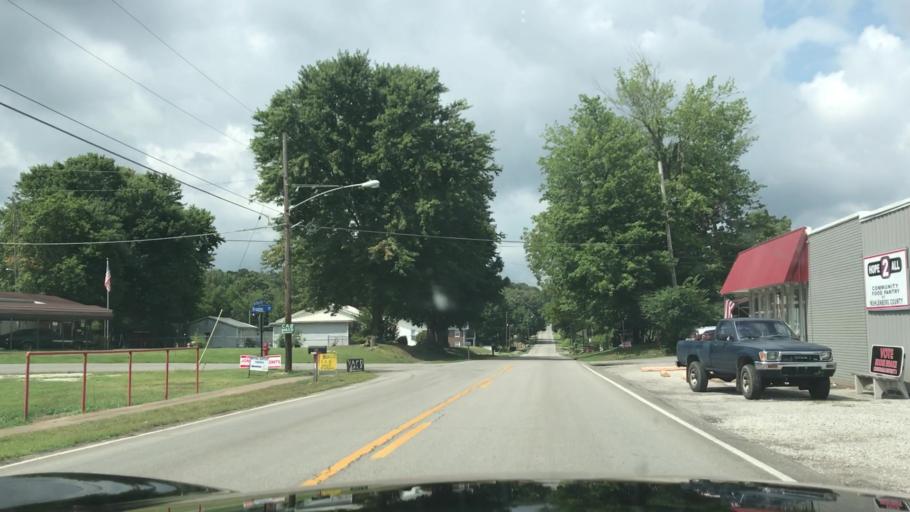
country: US
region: Kentucky
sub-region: Muhlenberg County
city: Central City
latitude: 37.2168
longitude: -87.0507
